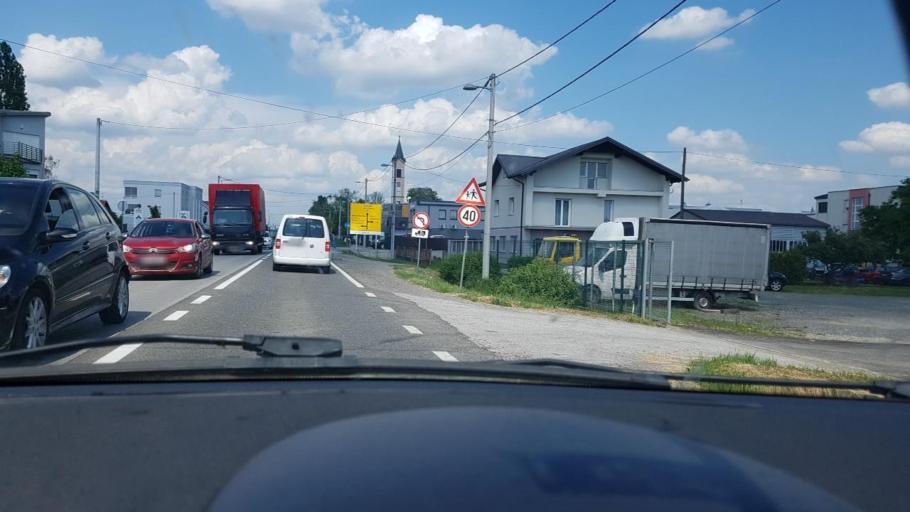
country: HR
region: Grad Zagreb
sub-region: Sesvete
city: Sesvete
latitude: 45.8623
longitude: 16.1522
